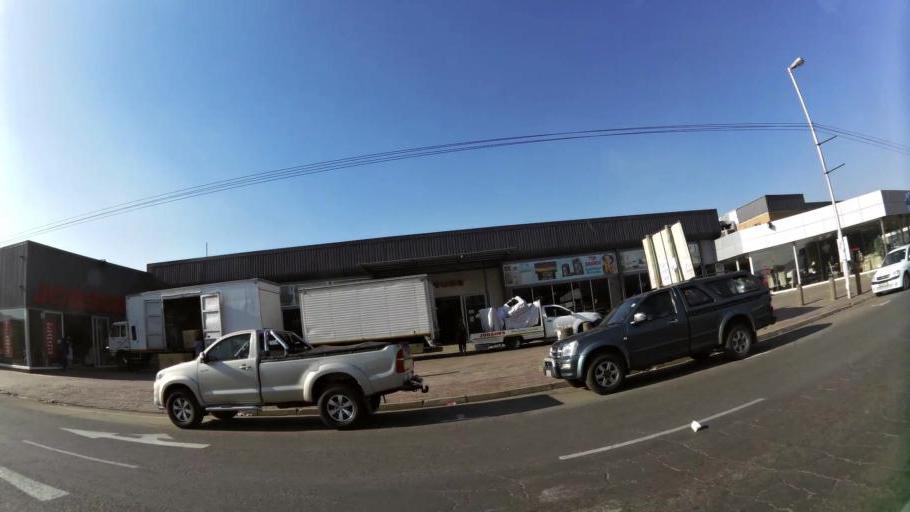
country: ZA
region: North-West
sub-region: Bojanala Platinum District Municipality
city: Rustenburg
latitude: -25.6693
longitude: 27.2399
